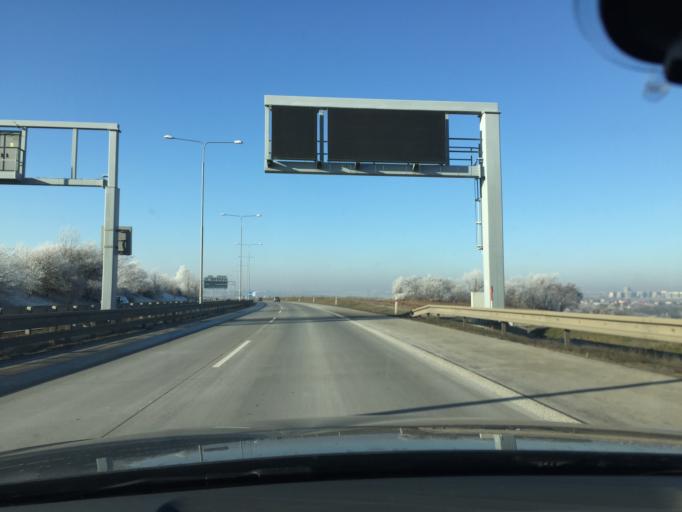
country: CZ
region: Central Bohemia
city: Trebotov
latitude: 50.0224
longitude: 14.3293
